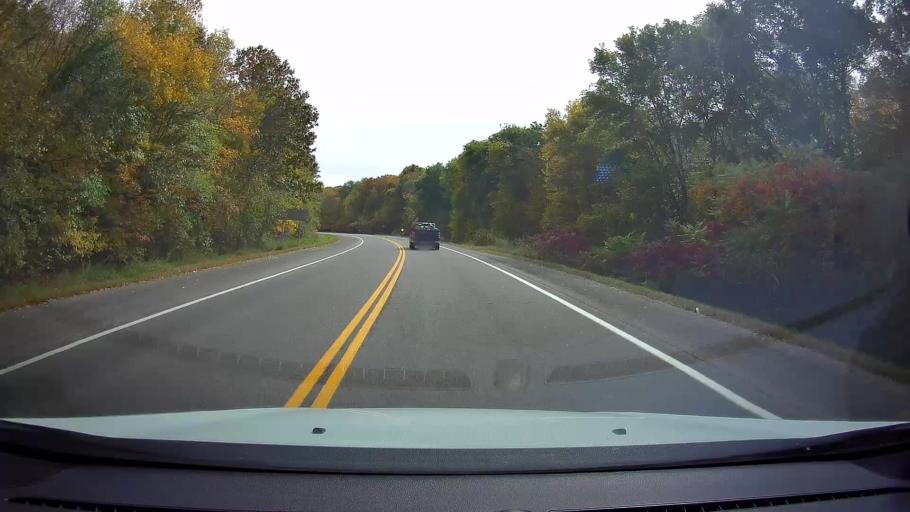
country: US
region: Wisconsin
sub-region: Polk County
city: Osceola
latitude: 45.3206
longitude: -92.7287
